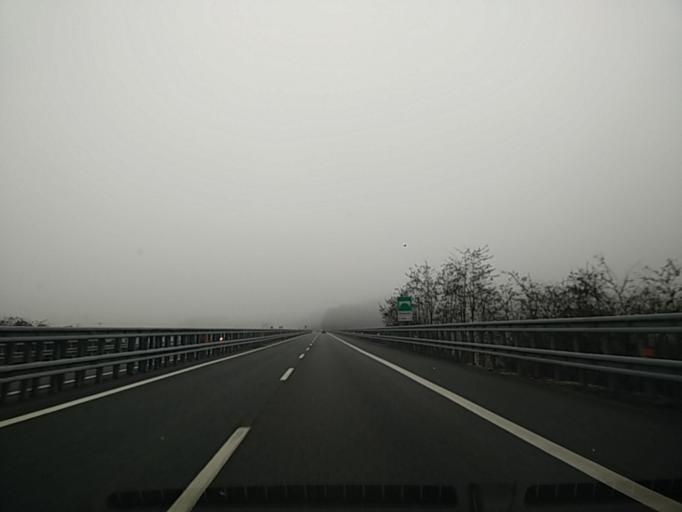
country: IT
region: Piedmont
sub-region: Provincia di Asti
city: San Paolo Solbrito
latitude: 44.9427
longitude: 7.9809
